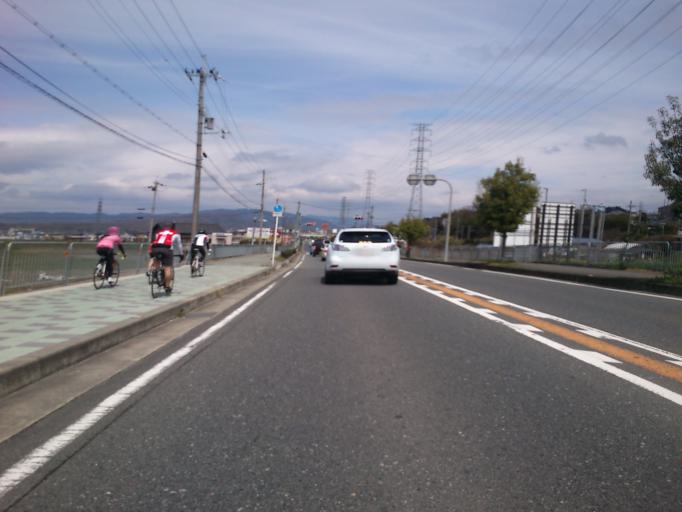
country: JP
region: Nara
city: Nara-shi
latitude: 34.7218
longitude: 135.8160
